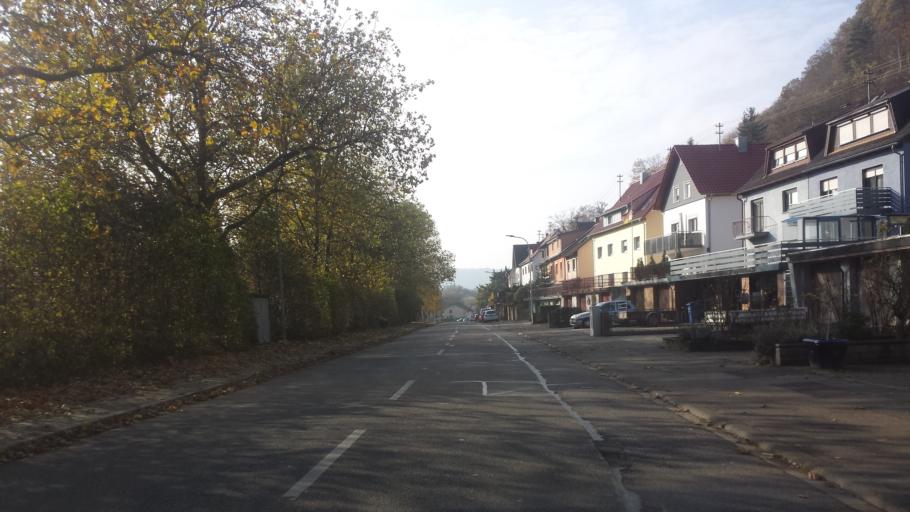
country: DE
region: Baden-Wuerttemberg
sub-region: Karlsruhe Region
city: Mosbach
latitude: 49.3478
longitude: 9.1273
